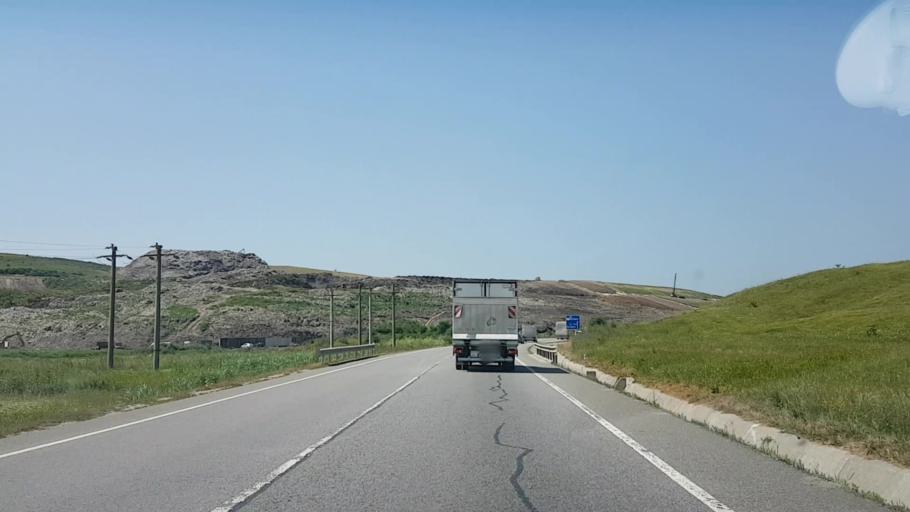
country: RO
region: Cluj
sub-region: Comuna Apahida
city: Dezmir
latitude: 46.7614
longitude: 23.6926
